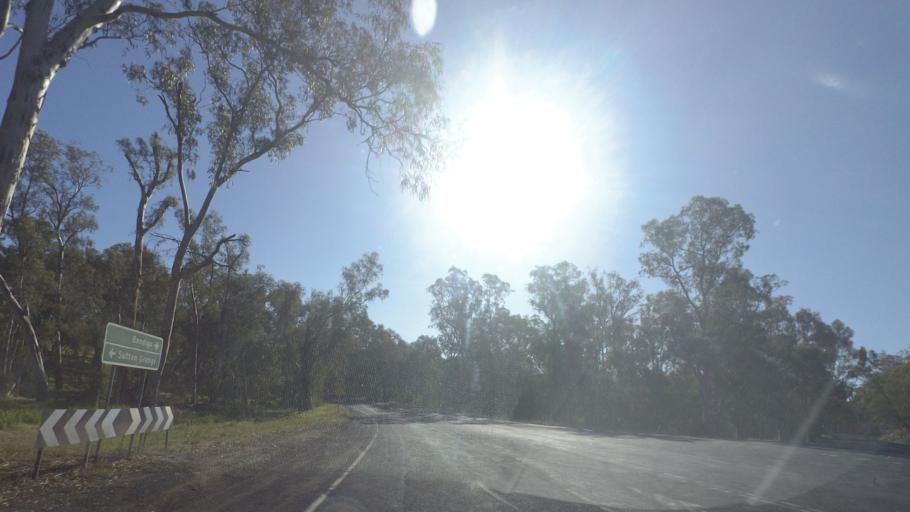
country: AU
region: Victoria
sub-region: Greater Bendigo
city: Kennington
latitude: -36.9222
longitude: 144.3441
